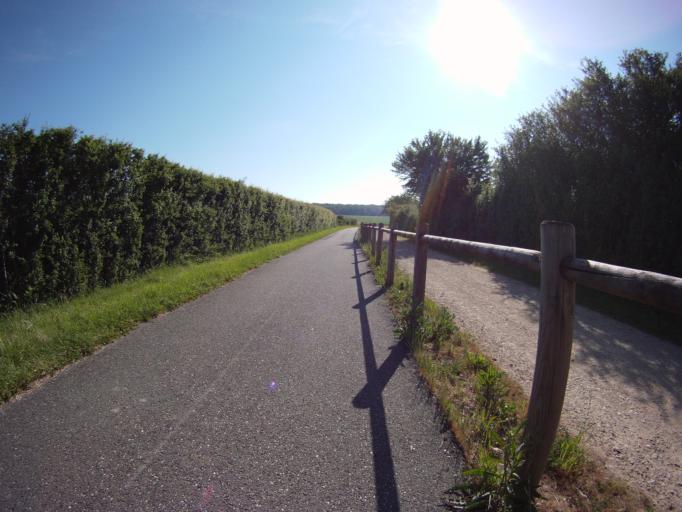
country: FR
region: Lorraine
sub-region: Departement de Meurthe-et-Moselle
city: Seichamps
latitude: 48.7418
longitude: 6.2986
